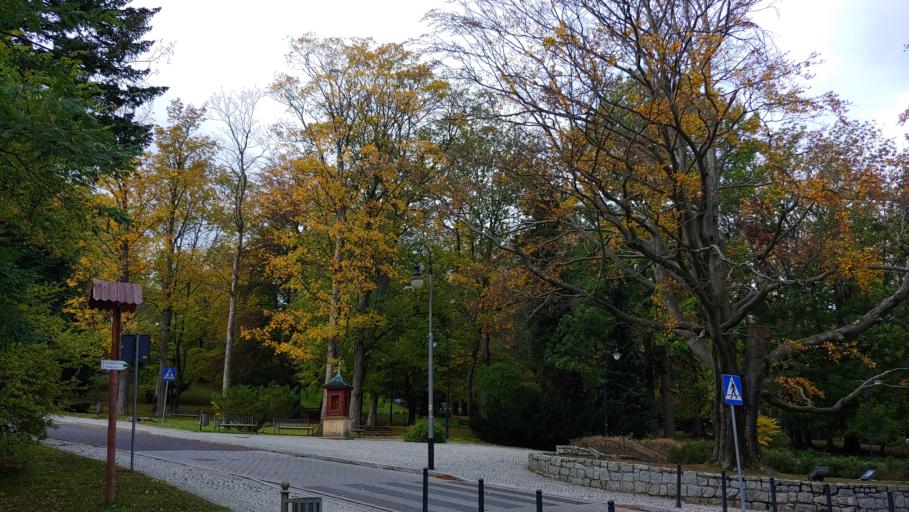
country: PL
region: Lower Silesian Voivodeship
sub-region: Powiat lubanski
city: Swieradow-Zdroj
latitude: 50.9072
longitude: 15.3344
